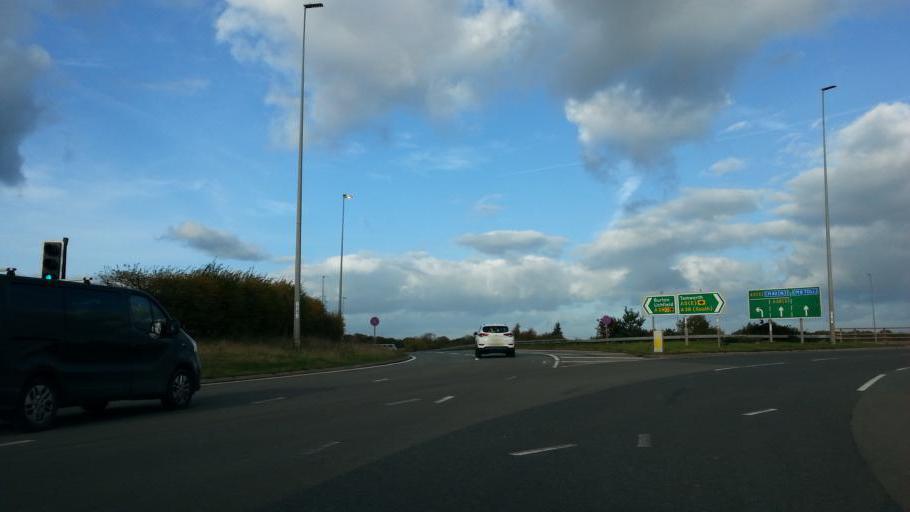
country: GB
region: England
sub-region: Staffordshire
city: Shenstone
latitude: 52.6405
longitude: -1.8054
